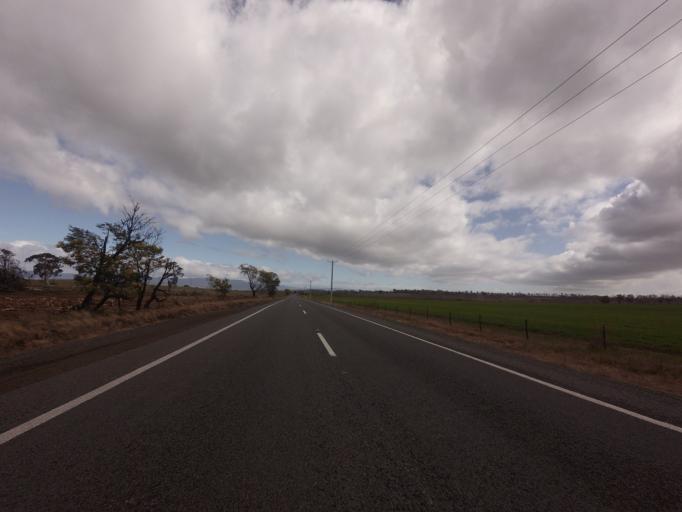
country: AU
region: Tasmania
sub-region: Northern Midlands
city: Evandale
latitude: -41.8345
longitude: 147.4594
